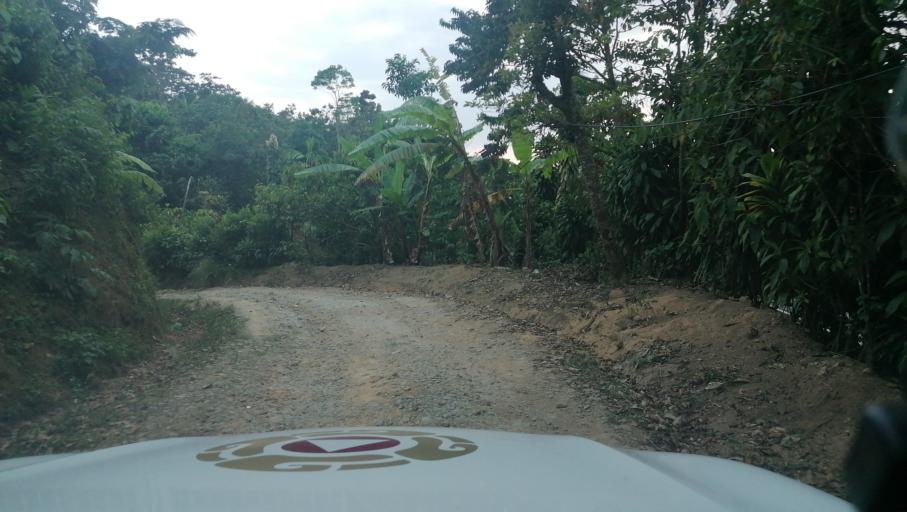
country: MX
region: Chiapas
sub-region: Cacahoatan
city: Benito Juarez
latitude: 15.1021
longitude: -92.2174
